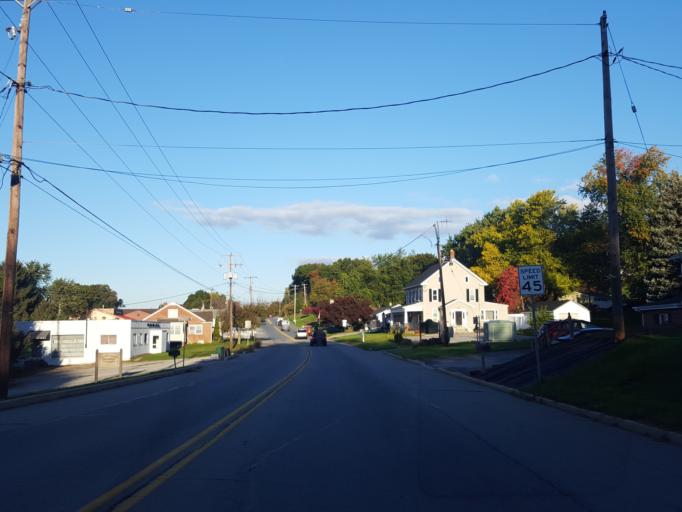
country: US
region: Pennsylvania
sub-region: York County
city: Red Lion
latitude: 39.9078
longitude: -76.6146
